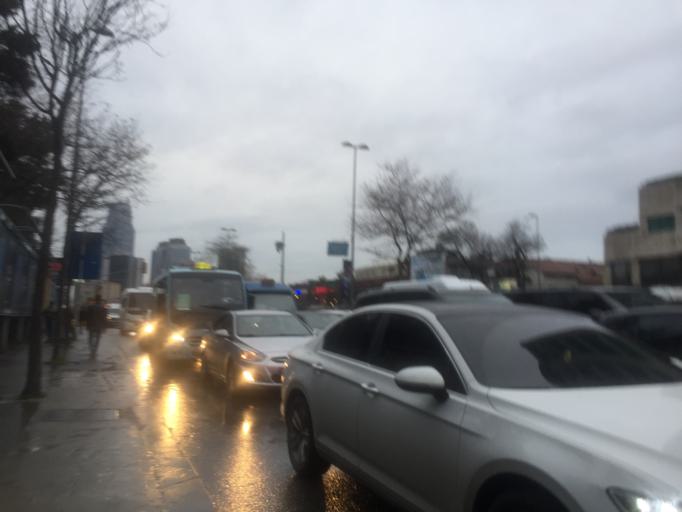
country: TR
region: Istanbul
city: Sisli
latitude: 41.0751
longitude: 29.0148
